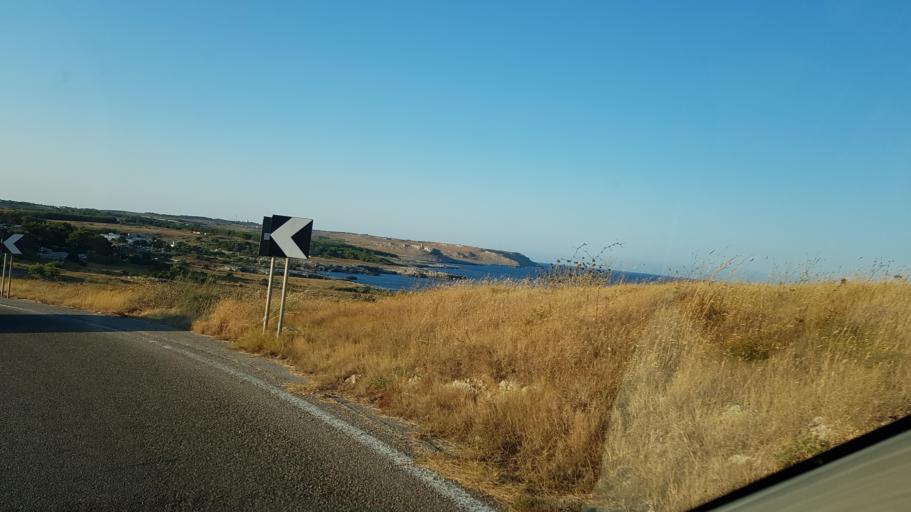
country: IT
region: Apulia
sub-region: Provincia di Lecce
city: Cerfignano
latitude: 40.0716
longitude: 18.4808
